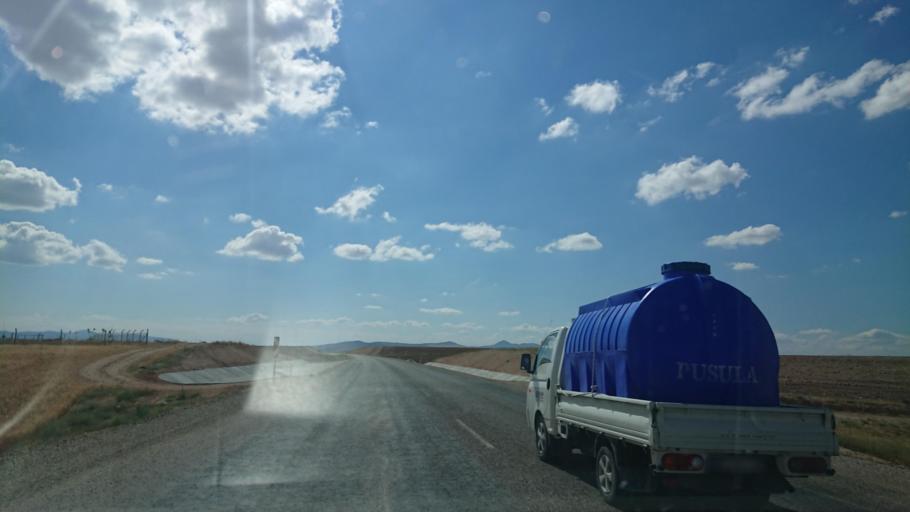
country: TR
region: Kirsehir
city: Kirsehir
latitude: 39.1237
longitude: 33.9943
